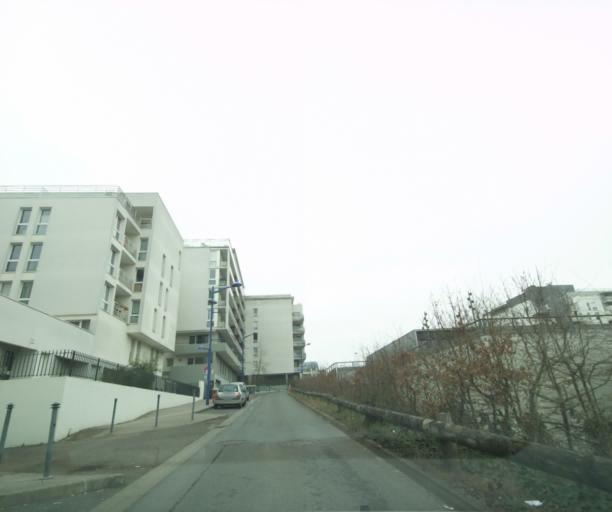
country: FR
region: Ile-de-France
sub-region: Departement du Val-d'Oise
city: Courdimanche
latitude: 49.0471
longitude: 2.0127
